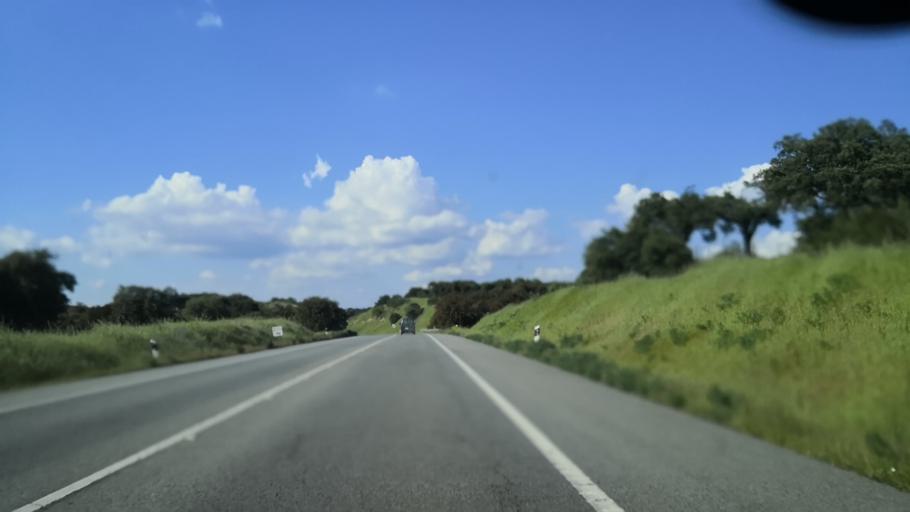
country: PT
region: Portalegre
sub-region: Arronches
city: Arronches
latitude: 39.0637
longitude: -7.4366
